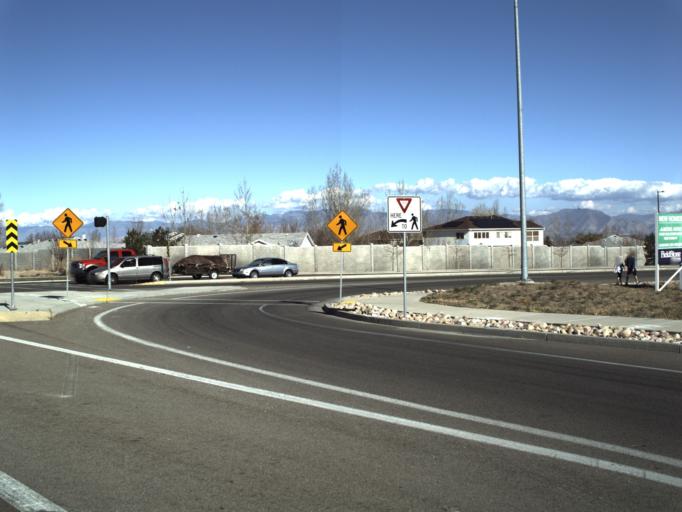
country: US
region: Utah
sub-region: Salt Lake County
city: Oquirrh
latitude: 40.5945
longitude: -112.0242
